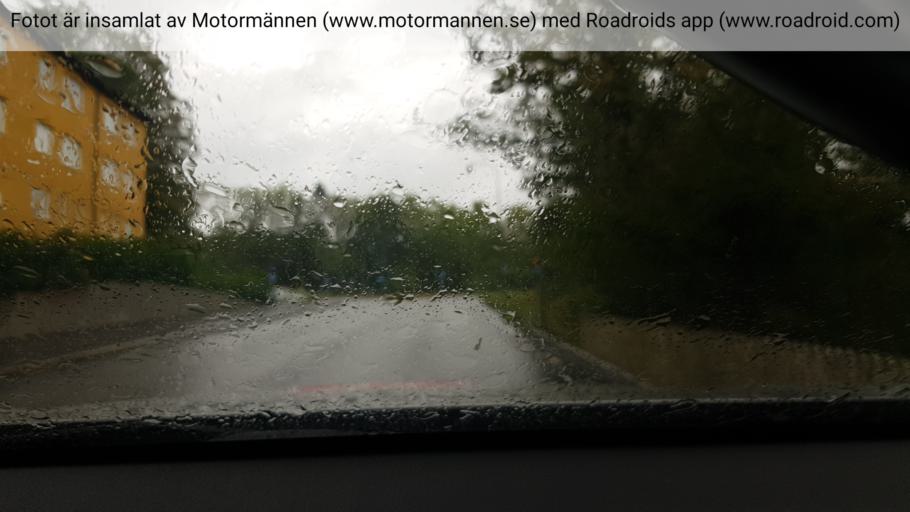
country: SE
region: Stockholm
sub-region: Haninge Kommun
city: Jordbro
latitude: 59.1036
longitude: 18.0471
